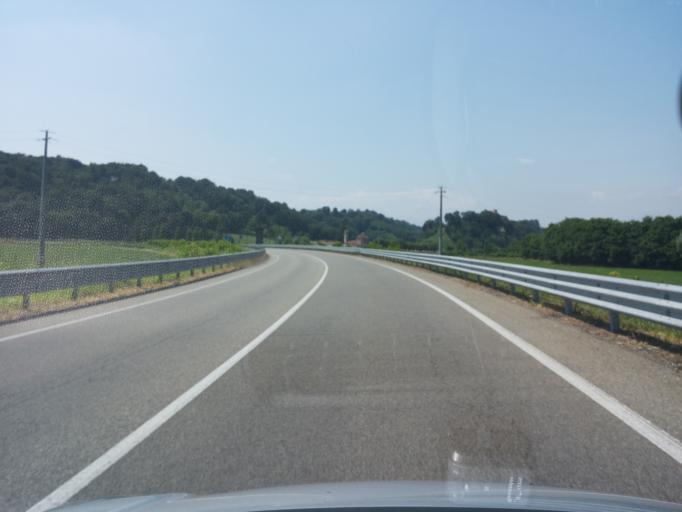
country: IT
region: Piedmont
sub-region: Provincia di Biella
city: Castelletto Cervo
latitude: 45.5258
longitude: 8.1973
